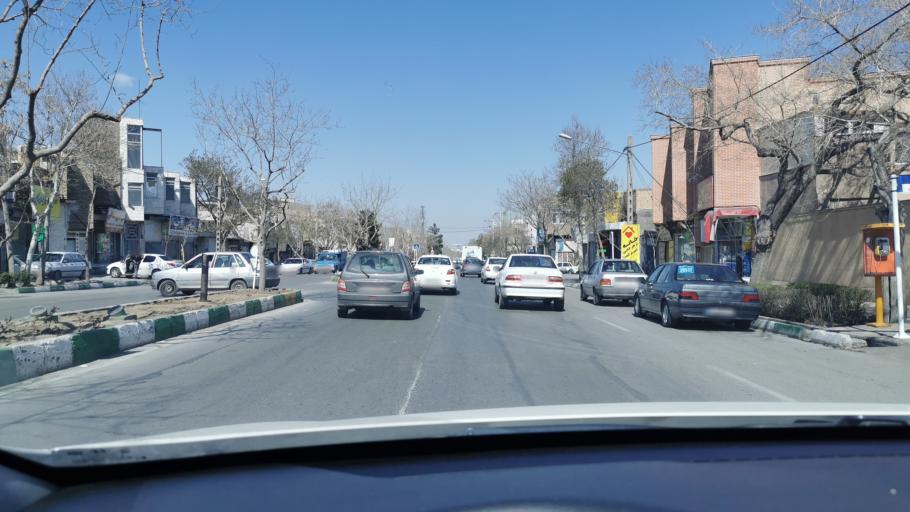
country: IR
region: Razavi Khorasan
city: Mashhad
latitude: 36.2716
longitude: 59.5757
